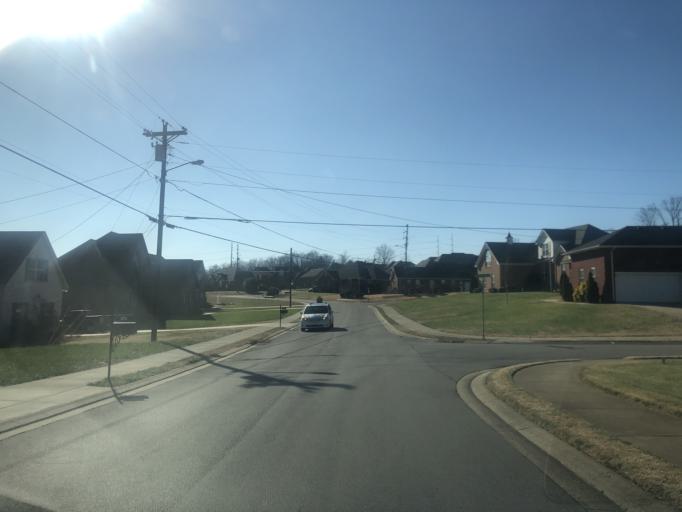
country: US
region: Tennessee
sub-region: Rutherford County
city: Smyrna
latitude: 35.9668
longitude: -86.5416
